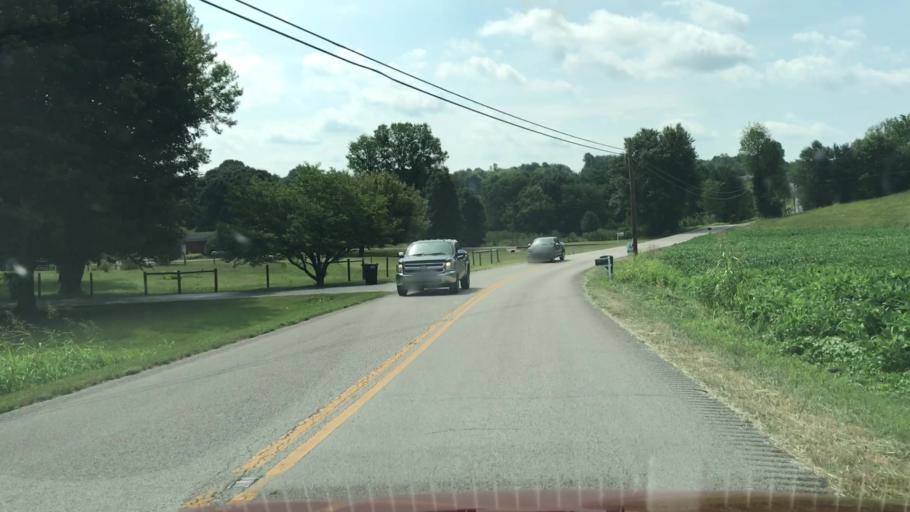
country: US
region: Kentucky
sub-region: Barren County
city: Glasgow
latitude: 36.9707
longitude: -85.8936
